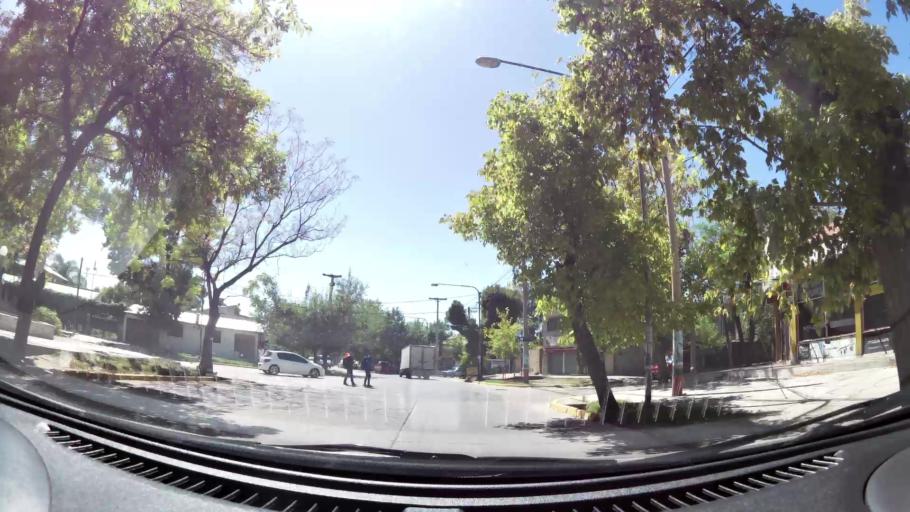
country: AR
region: Mendoza
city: Mendoza
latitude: -32.8833
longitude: -68.8135
